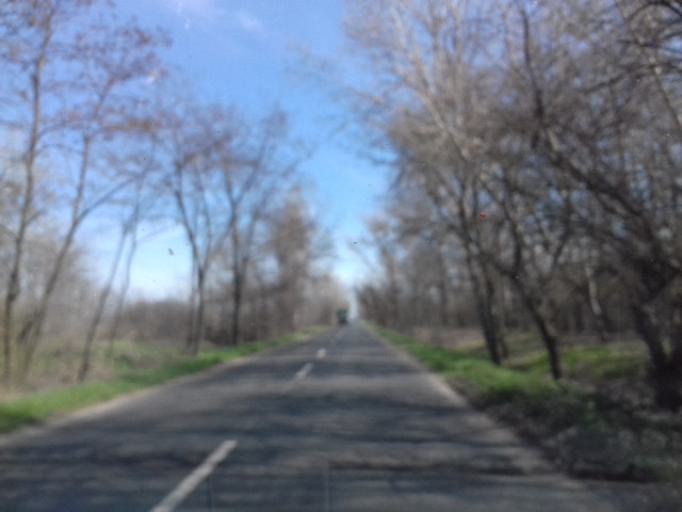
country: HU
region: Bacs-Kiskun
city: Kecskemet
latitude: 46.8924
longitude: 19.7374
